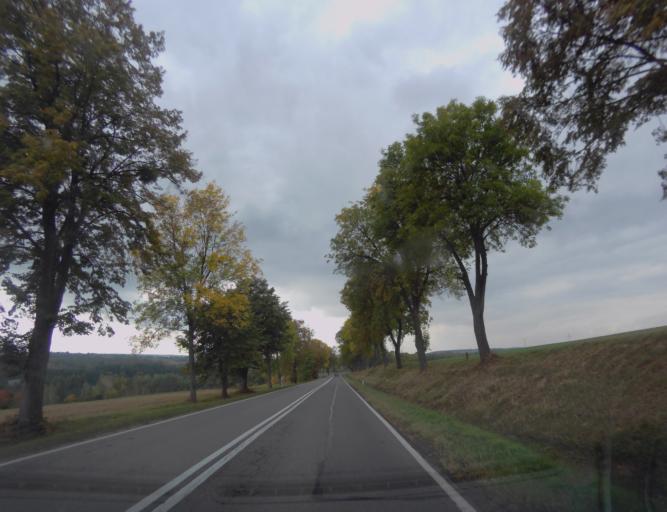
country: PL
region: Lublin Voivodeship
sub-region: Powiat krasnostawski
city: Zolkiewka
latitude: 50.9198
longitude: 22.8741
